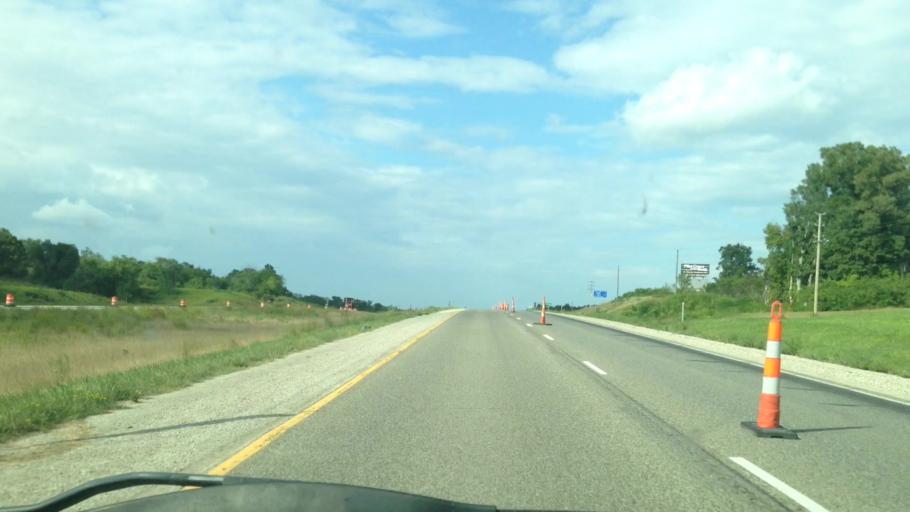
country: US
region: Iowa
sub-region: Henry County
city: Mount Pleasant
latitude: 40.9096
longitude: -91.5474
